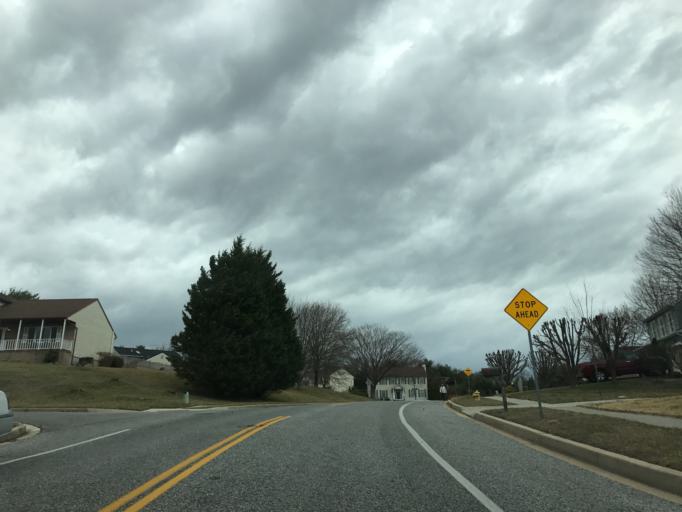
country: US
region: Maryland
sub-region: Harford County
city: South Bel Air
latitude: 39.5307
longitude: -76.3224
